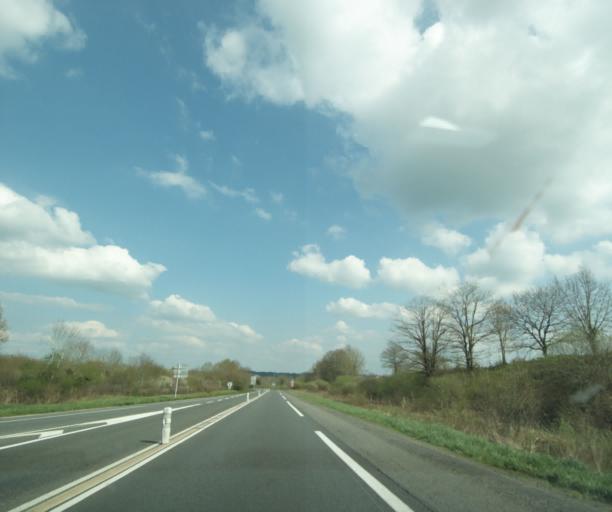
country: FR
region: Auvergne
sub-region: Departement de l'Allier
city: Buxieres-les-Mines
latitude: 46.3998
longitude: 3.0520
